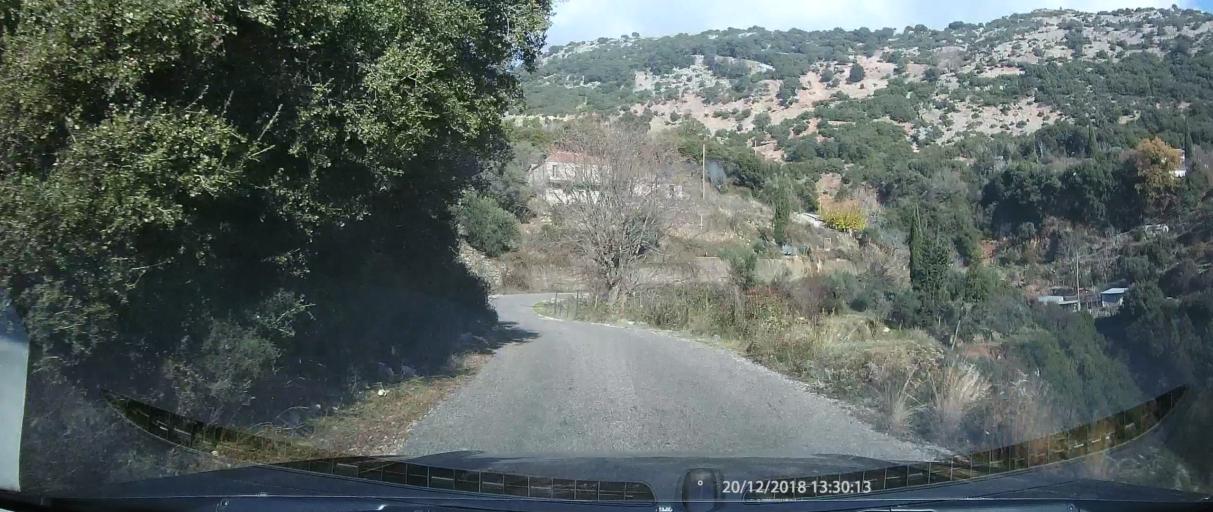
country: GR
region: West Greece
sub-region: Nomos Aitolias kai Akarnanias
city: Paravola
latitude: 38.6328
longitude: 21.5823
